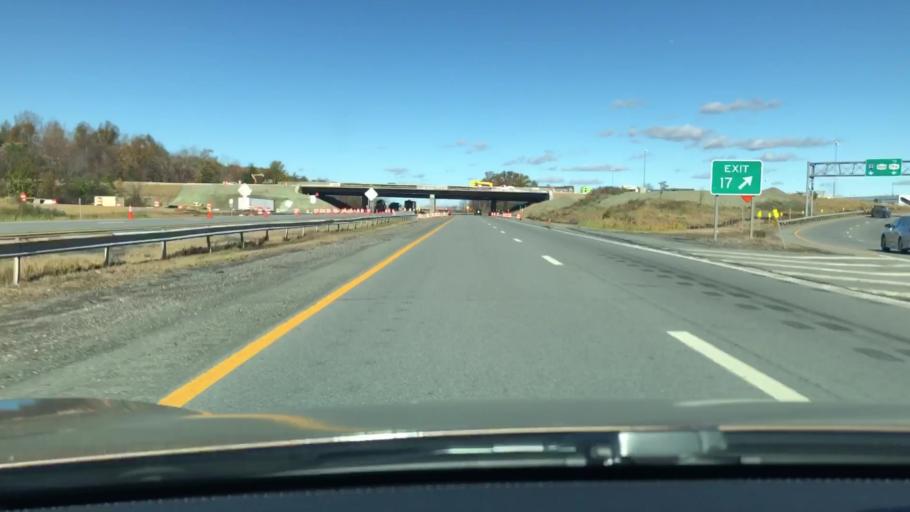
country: US
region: New York
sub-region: Orange County
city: Gardnertown
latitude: 41.5079
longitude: -74.0748
